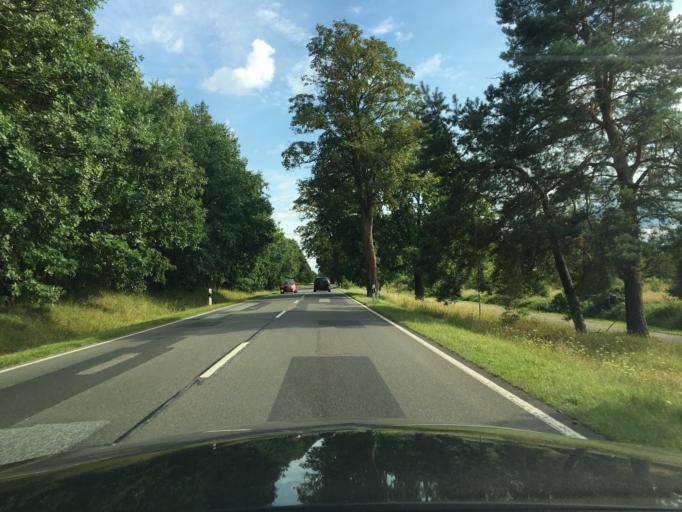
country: DE
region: Mecklenburg-Vorpommern
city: Neustrelitz
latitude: 53.4051
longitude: 13.0426
